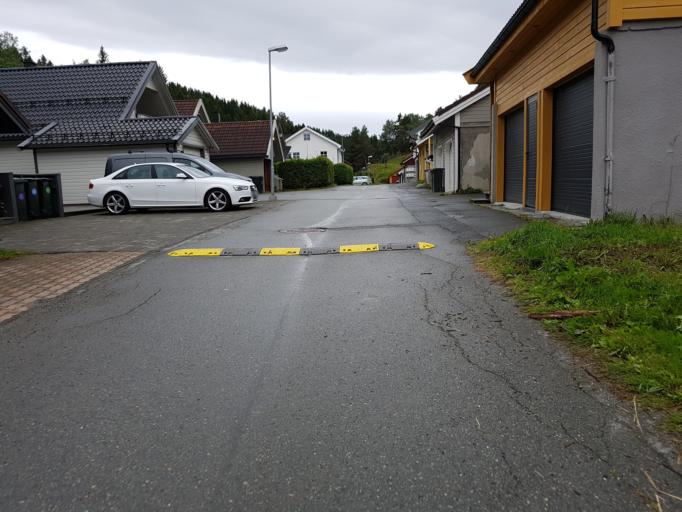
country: NO
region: Sor-Trondelag
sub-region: Trondheim
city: Trondheim
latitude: 63.4068
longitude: 10.4854
